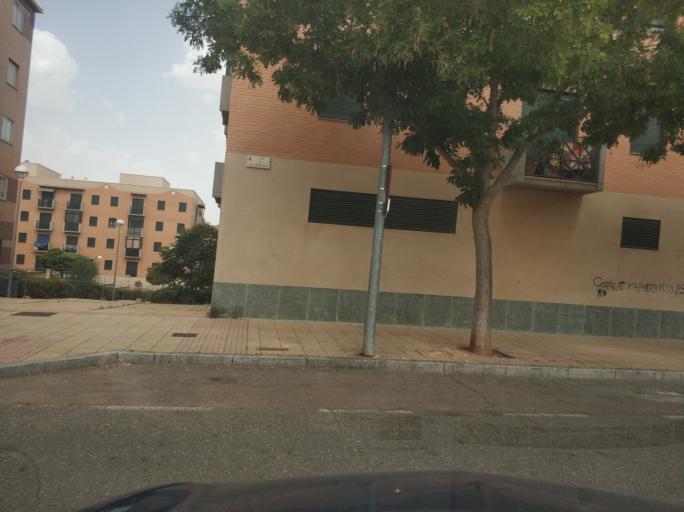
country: ES
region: Castille and Leon
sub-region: Provincia de Salamanca
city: Aldeatejada
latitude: 40.9519
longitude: -5.6938
